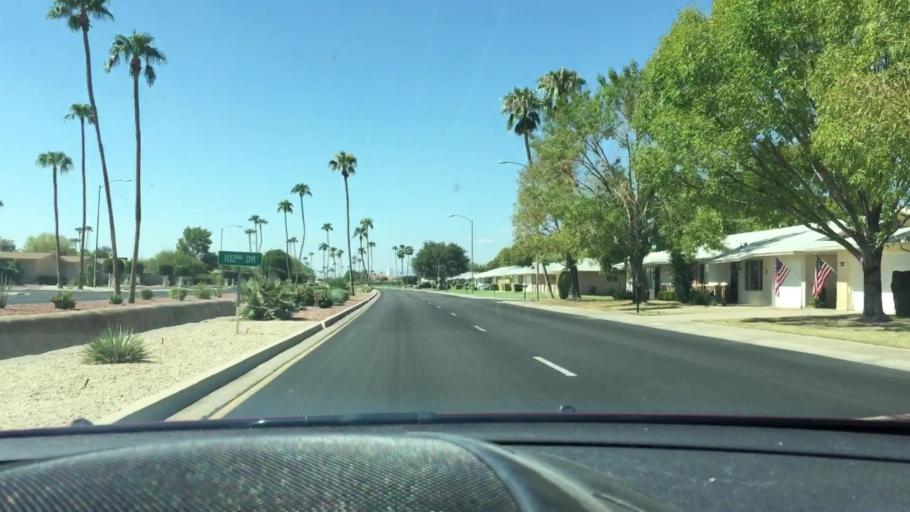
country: US
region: Arizona
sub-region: Maricopa County
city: Sun City
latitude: 33.6456
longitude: -112.2797
